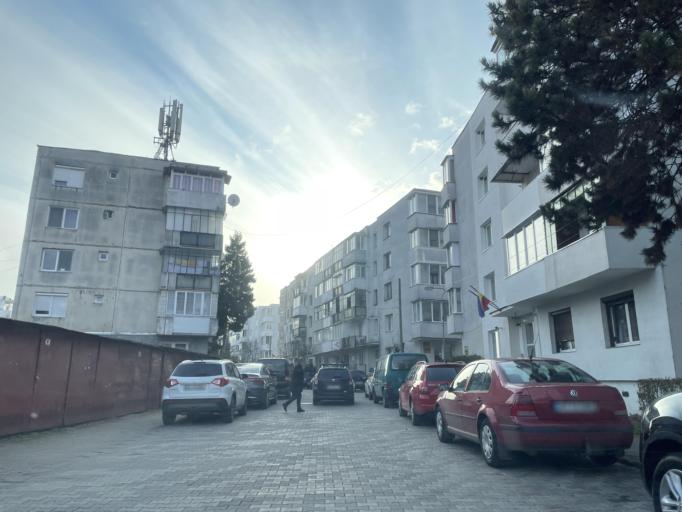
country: RO
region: Mures
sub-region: Municipiul Reghin
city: Reghin
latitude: 46.7841
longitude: 24.6991
